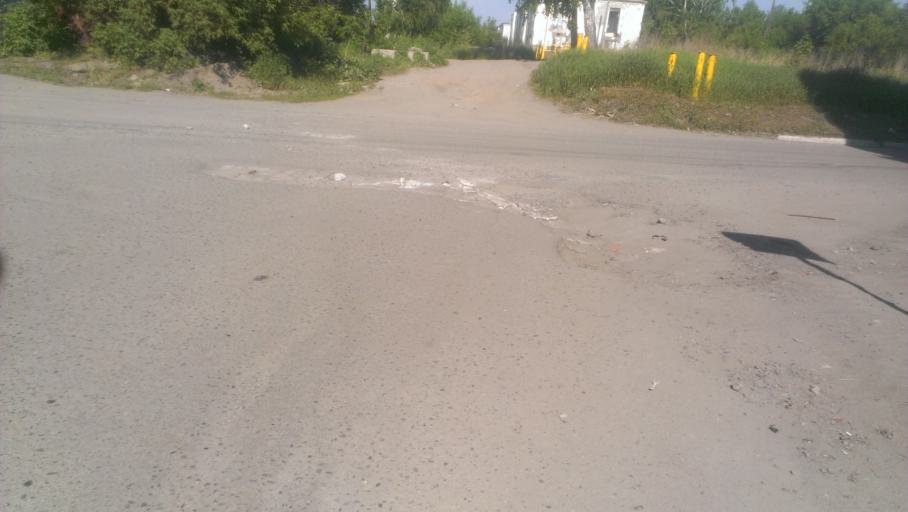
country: RU
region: Altai Krai
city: Novoaltaysk
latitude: 53.3950
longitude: 83.9364
